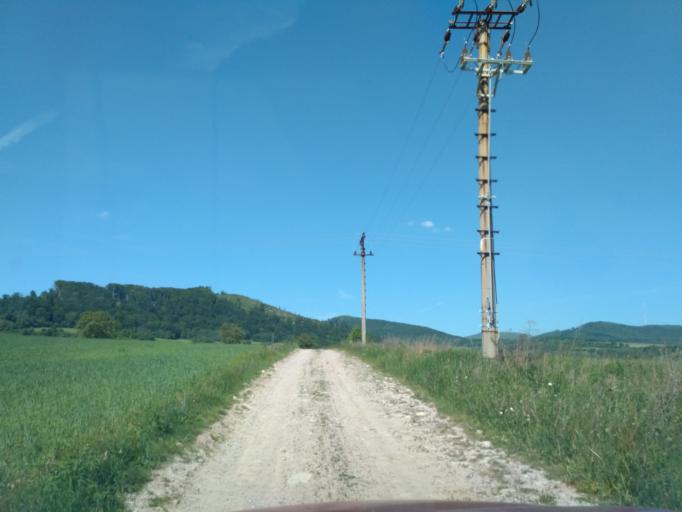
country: SK
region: Presovsky
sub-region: Okres Presov
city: Presov
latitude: 48.8934
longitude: 21.3934
